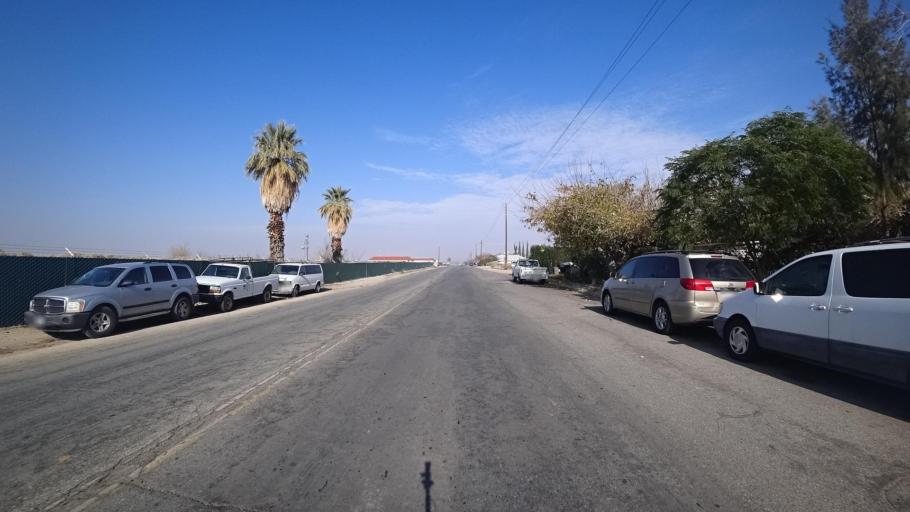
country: US
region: California
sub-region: Kern County
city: Ford City
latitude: 35.1531
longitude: -119.4652
